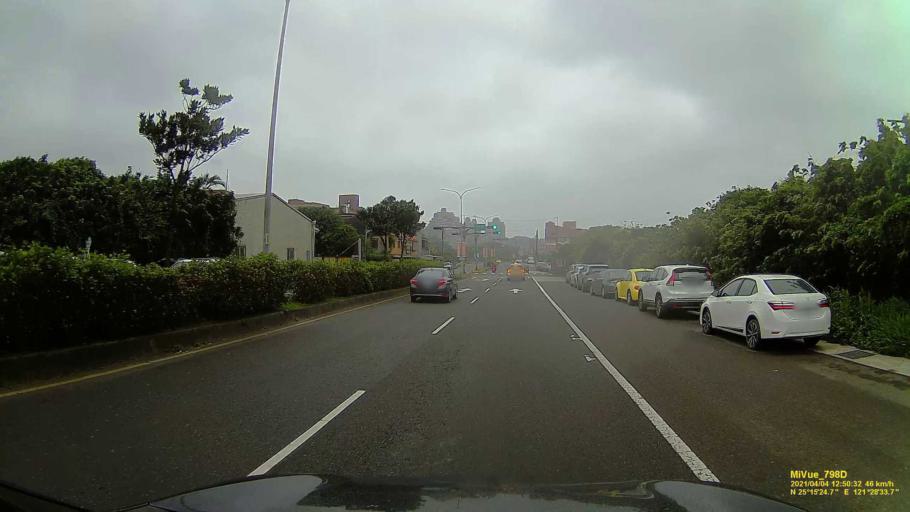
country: TW
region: Taipei
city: Taipei
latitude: 25.2568
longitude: 121.4760
